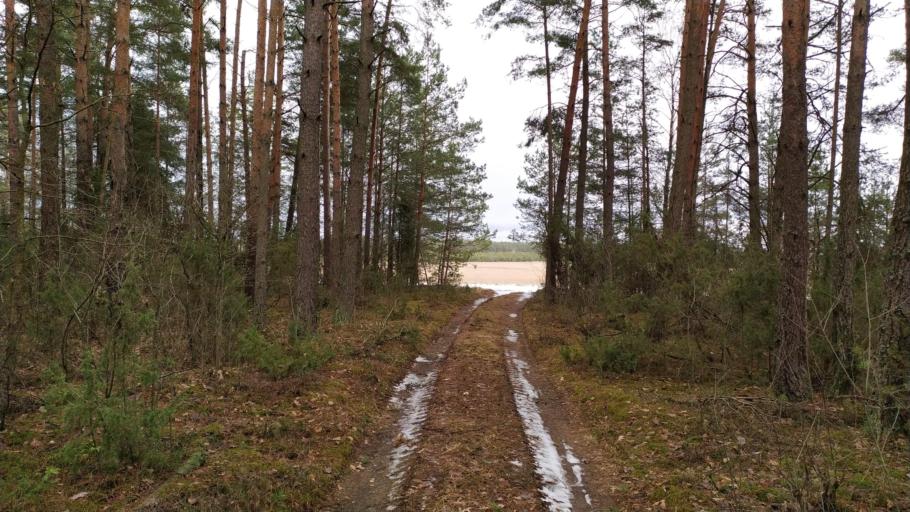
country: BY
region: Brest
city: Kamyanyets
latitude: 52.4358
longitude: 23.9998
